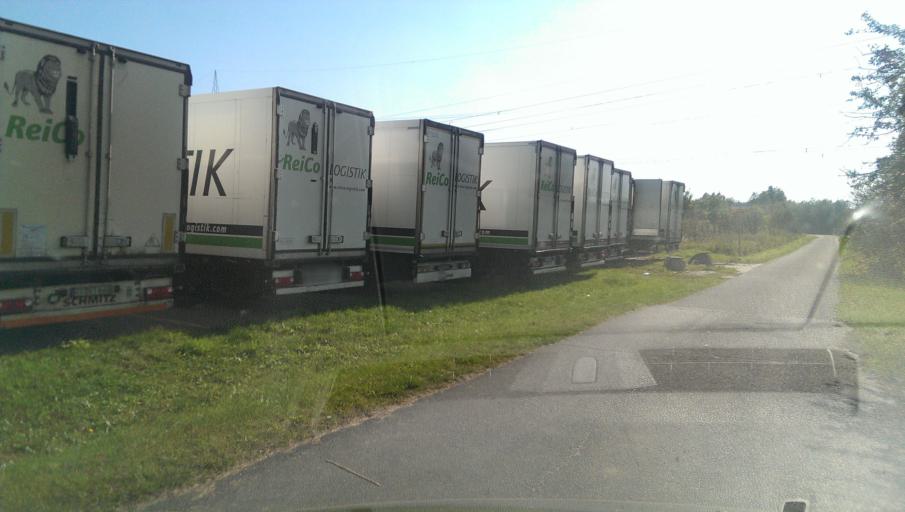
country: DE
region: Brandenburg
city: Trebbin
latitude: 52.2254
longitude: 13.3148
